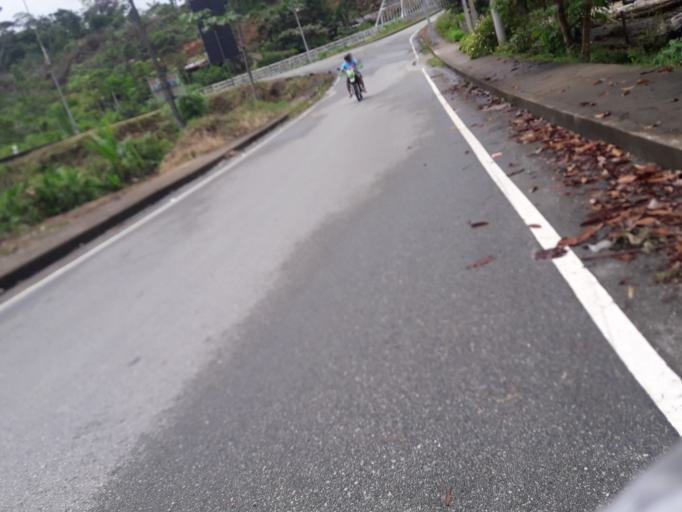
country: EC
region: Napo
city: Tena
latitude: -0.9579
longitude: -77.8613
